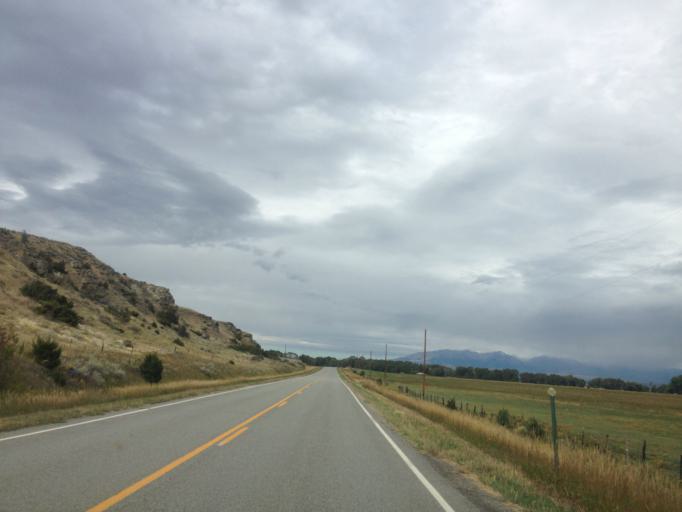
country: US
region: Montana
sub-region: Sweet Grass County
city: Big Timber
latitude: 45.7816
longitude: -109.8245
